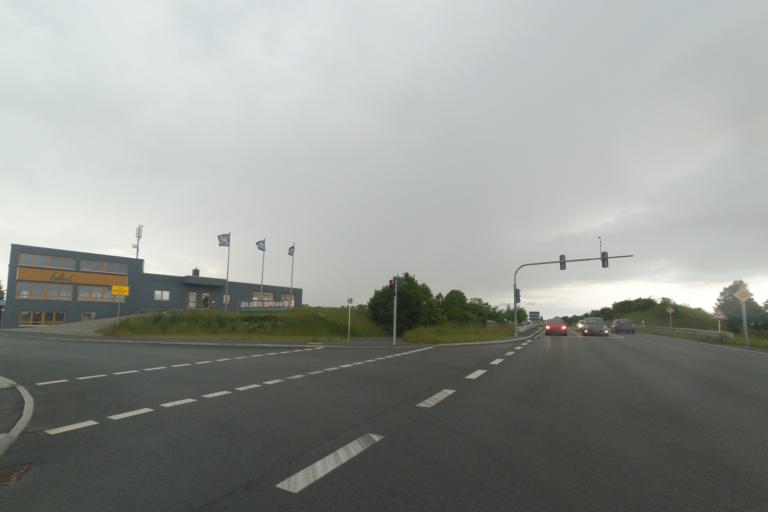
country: DE
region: Bavaria
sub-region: Upper Franconia
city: Helmbrechts
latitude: 50.2322
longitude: 11.7343
